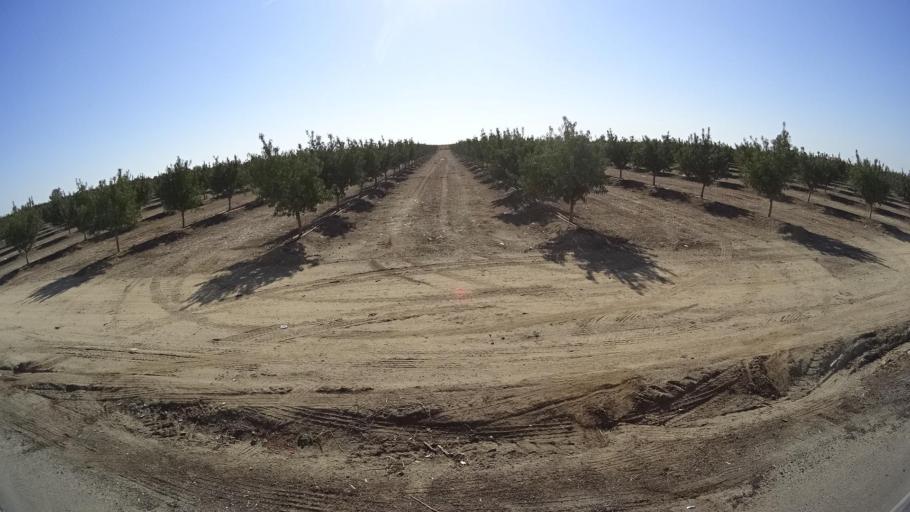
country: US
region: California
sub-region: Kern County
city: McFarland
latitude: 35.7180
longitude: -119.1574
